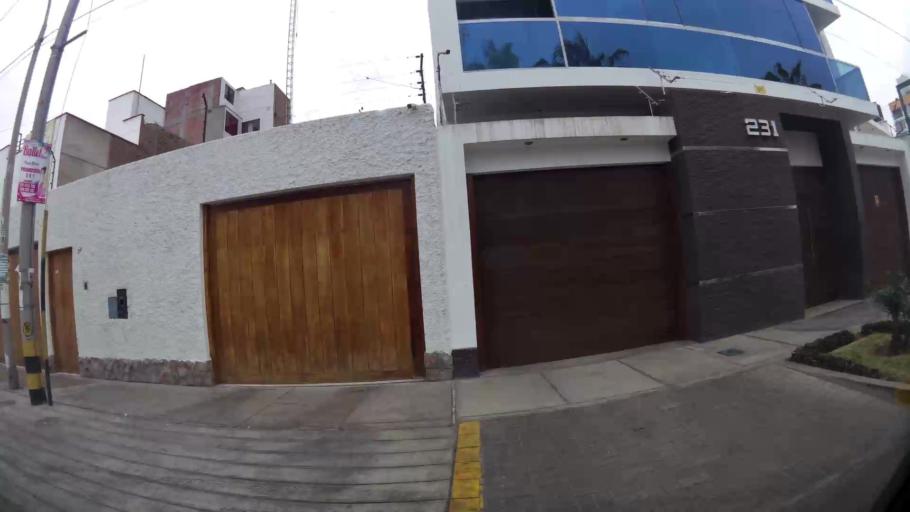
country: PE
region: La Libertad
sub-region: Provincia de Trujillo
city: Trujillo
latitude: -8.1189
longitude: -79.0312
